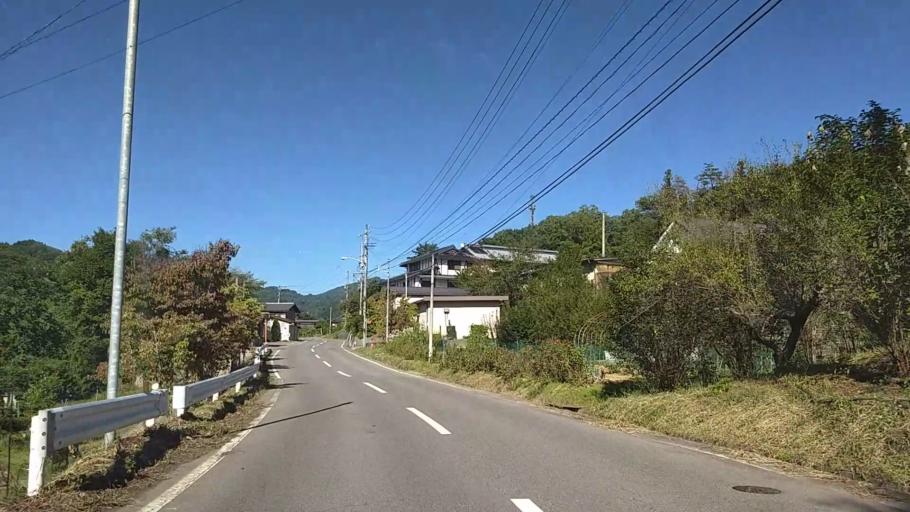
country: JP
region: Nagano
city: Nagano-shi
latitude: 36.6124
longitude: 138.0895
